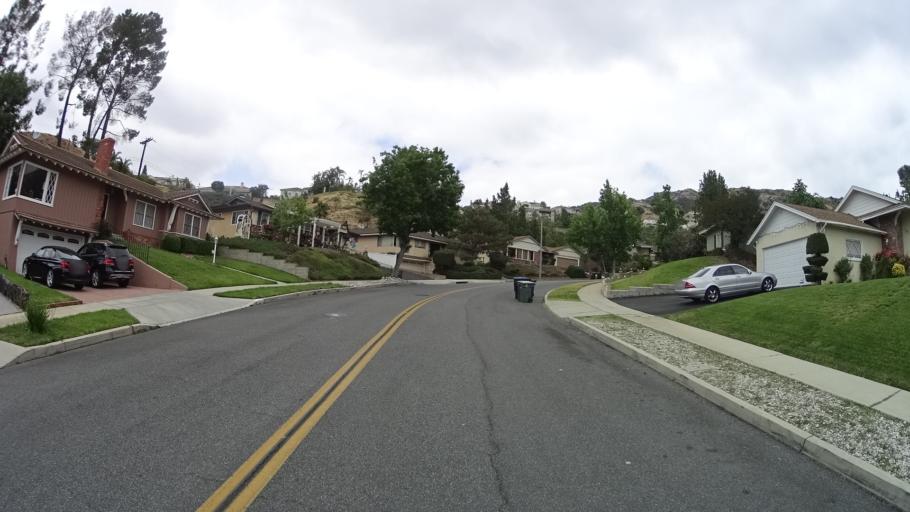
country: US
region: California
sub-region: Los Angeles County
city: Burbank
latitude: 34.2132
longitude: -118.3328
